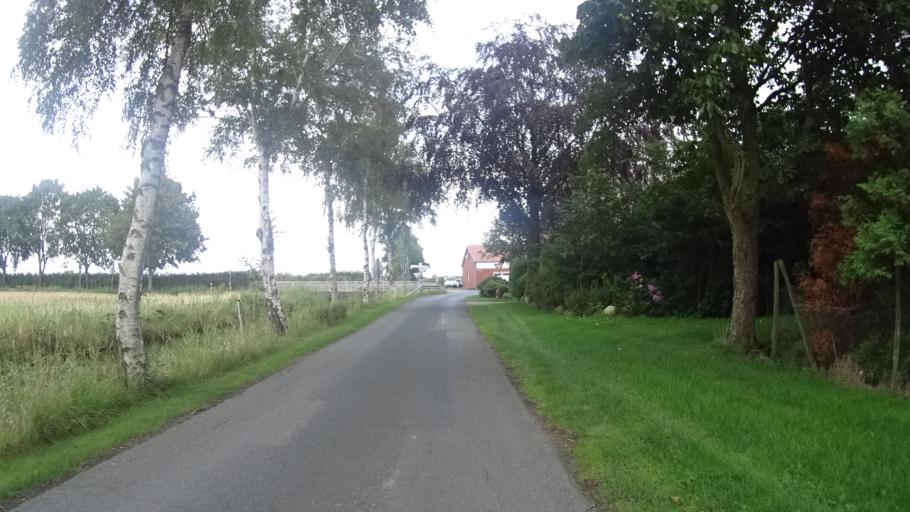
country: DE
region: Lower Saxony
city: Grossenworden
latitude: 53.7019
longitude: 9.2537
